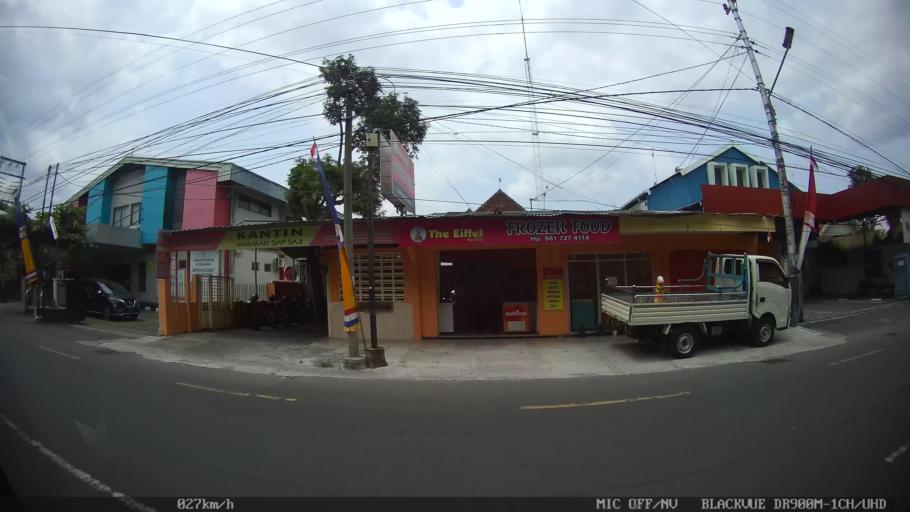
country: ID
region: Daerah Istimewa Yogyakarta
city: Yogyakarta
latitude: -7.8015
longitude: 110.3954
